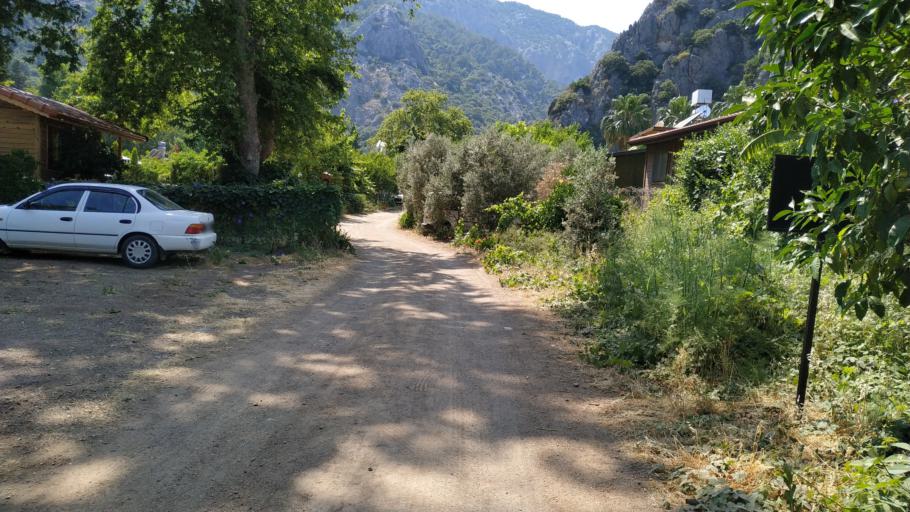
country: TR
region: Antalya
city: Tekirova
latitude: 36.4044
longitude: 30.4751
